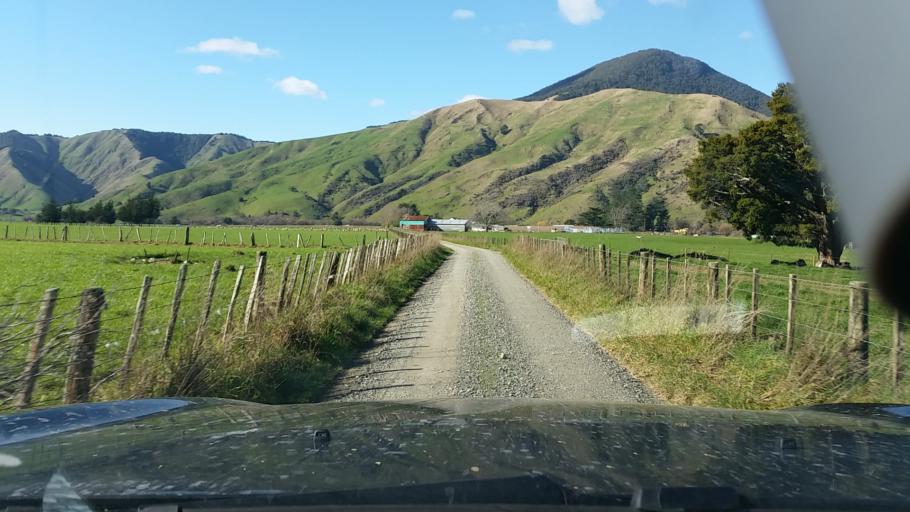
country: NZ
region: Marlborough
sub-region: Marlborough District
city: Picton
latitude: -41.3192
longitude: 173.7565
